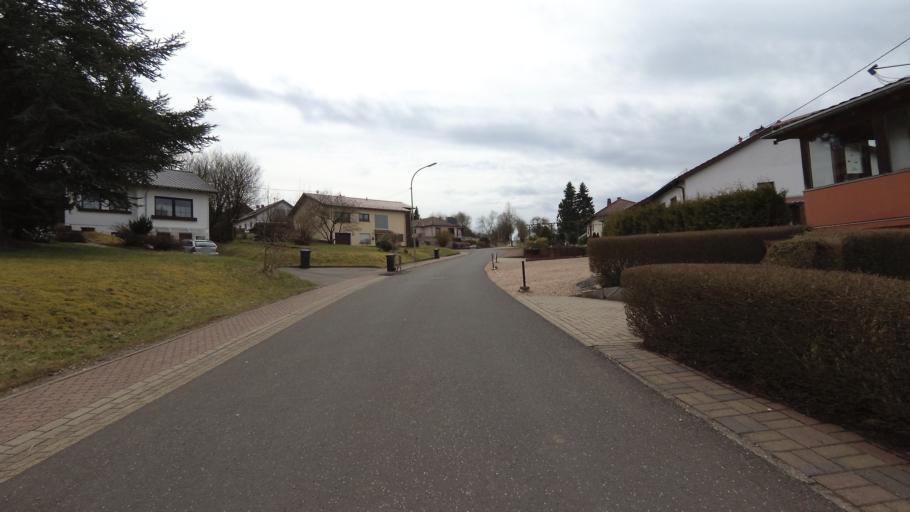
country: DE
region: Saarland
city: Mainzweiler
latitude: 49.4196
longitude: 7.1124
